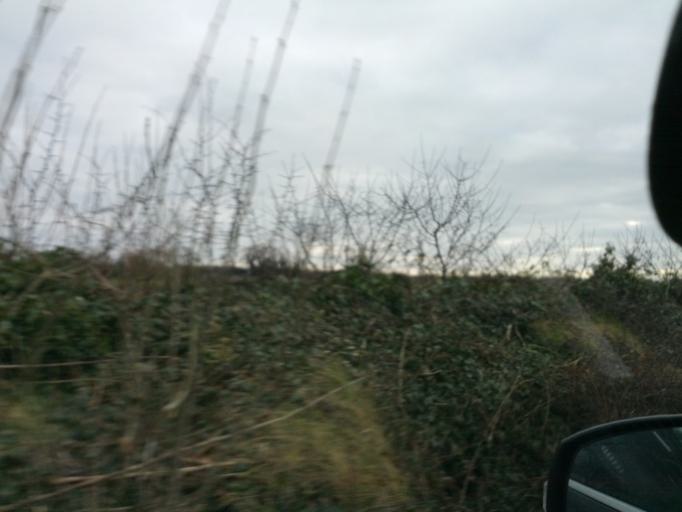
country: IE
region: Connaught
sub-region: County Galway
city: Athenry
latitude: 53.2180
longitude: -8.8103
